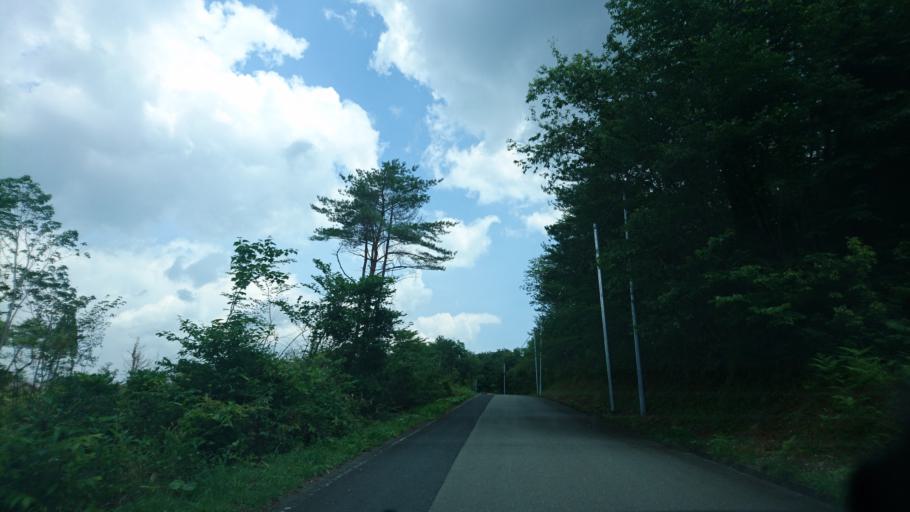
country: JP
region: Iwate
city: Ichinoseki
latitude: 38.9140
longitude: 141.2135
